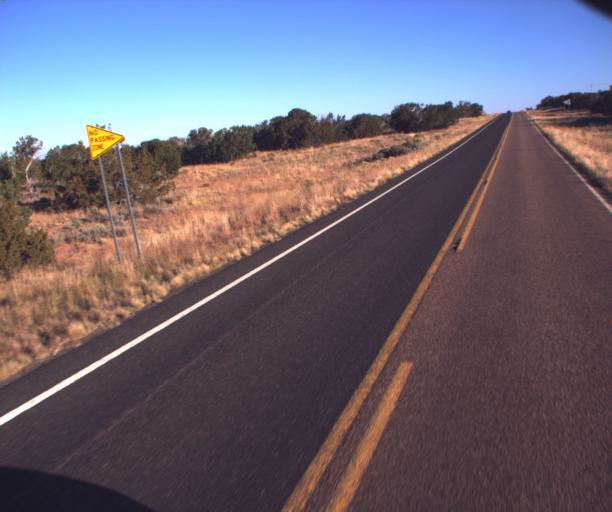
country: US
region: Arizona
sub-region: Apache County
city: Ganado
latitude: 35.4437
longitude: -109.5222
